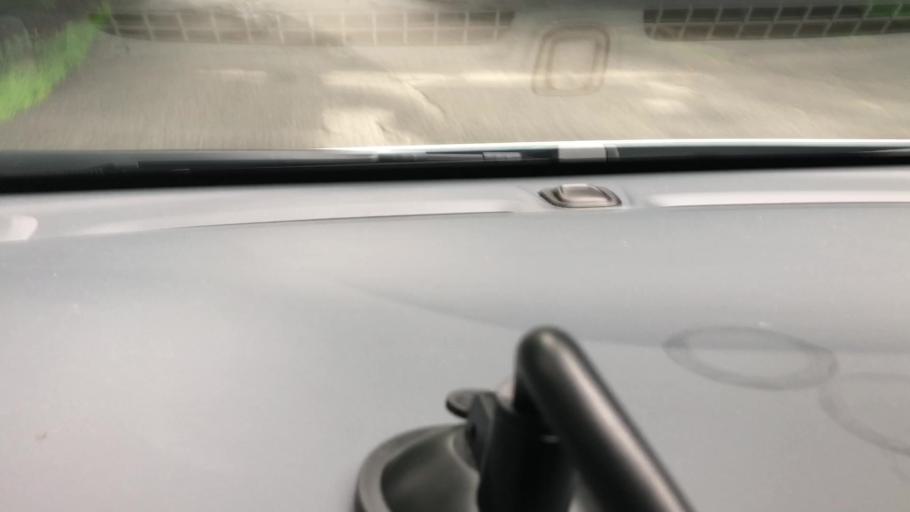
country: US
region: New Hampshire
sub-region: Hillsborough County
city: Pinardville
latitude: 42.9933
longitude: -71.5178
